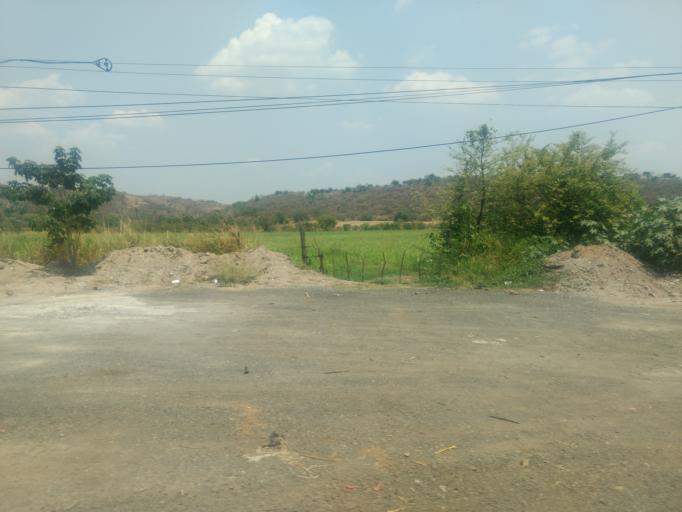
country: MX
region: Morelos
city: Puente de Ixtla
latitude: 18.6333
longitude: -99.3205
